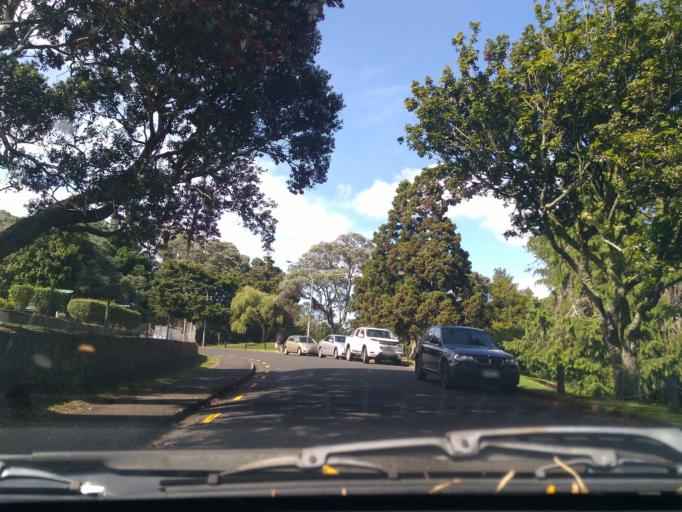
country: NZ
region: Auckland
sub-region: Auckland
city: Auckland
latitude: -36.8744
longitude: 174.7303
